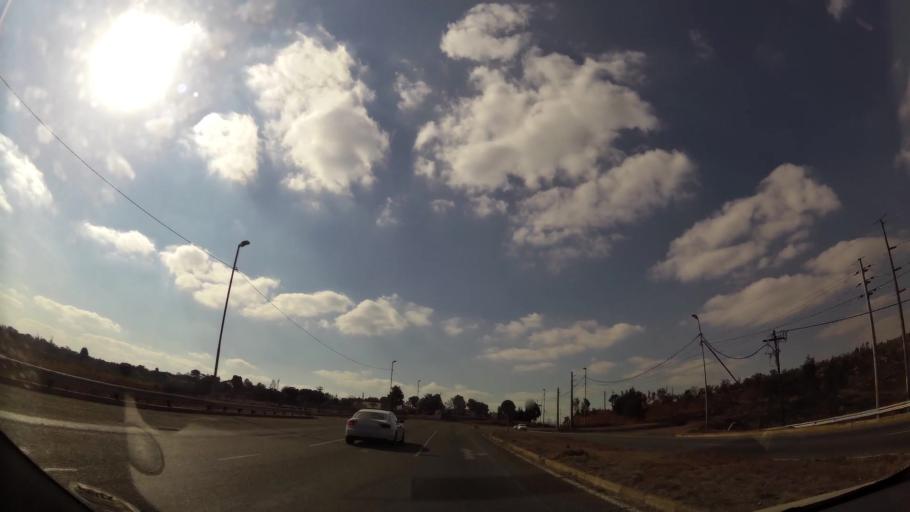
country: ZA
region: Gauteng
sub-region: West Rand District Municipality
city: Krugersdorp
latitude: -26.0650
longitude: 27.8056
